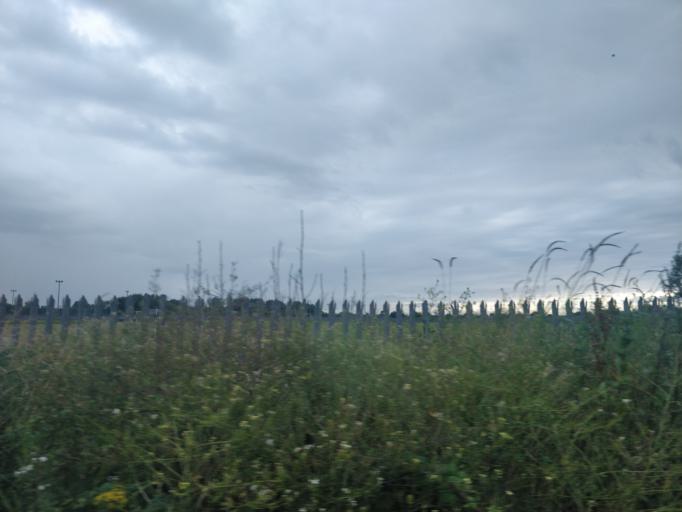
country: GB
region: England
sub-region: Sefton
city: Southport
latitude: 53.6717
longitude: -2.9748
